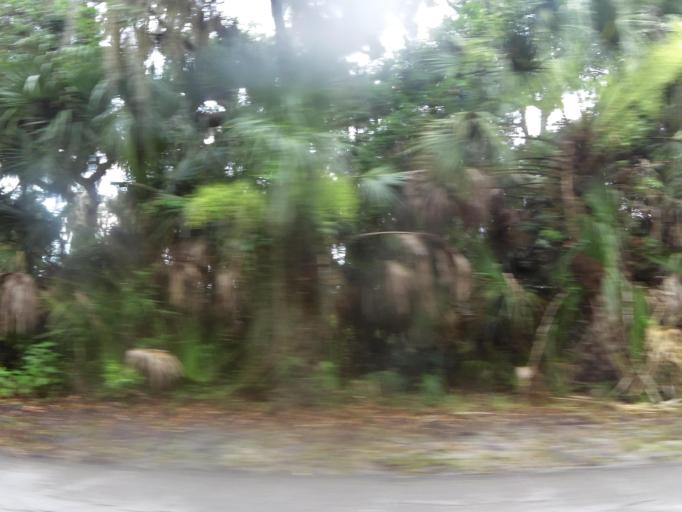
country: US
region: Florida
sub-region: Nassau County
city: Fernandina Beach
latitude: 30.6762
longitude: -81.4352
